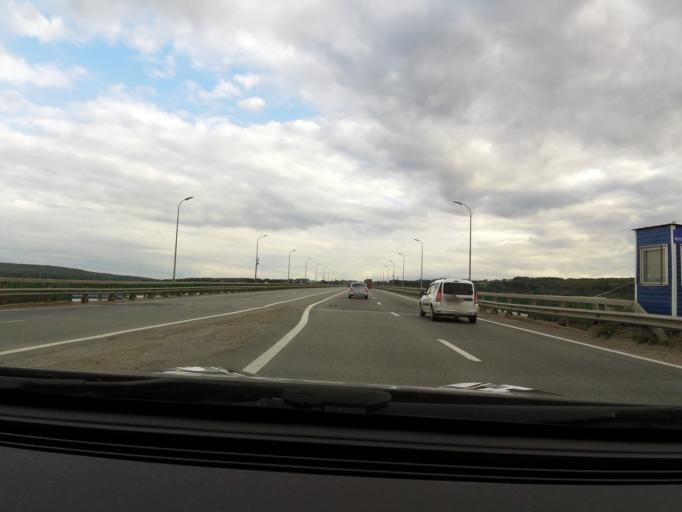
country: RU
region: Tatarstan
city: Osinovo
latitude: 55.7907
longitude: 48.8408
